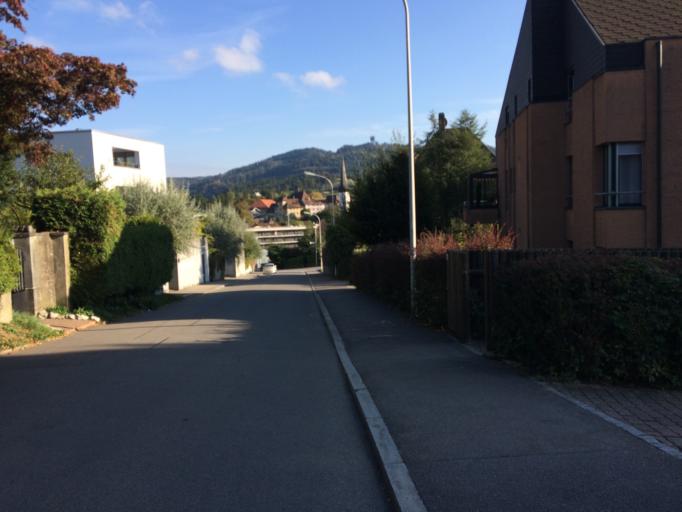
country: CH
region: Bern
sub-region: Bern-Mittelland District
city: Koniz
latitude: 46.9240
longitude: 7.4100
